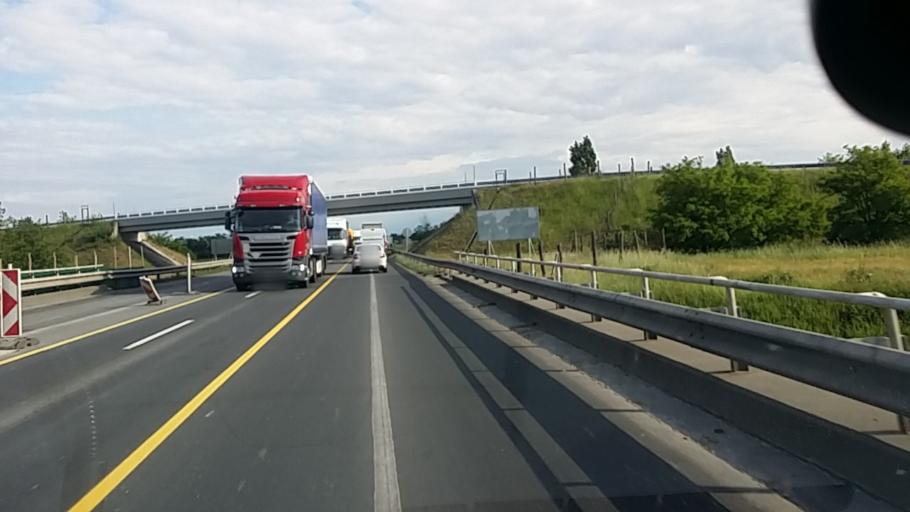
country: HU
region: Gyor-Moson-Sopron
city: Rajka
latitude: 47.9240
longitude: 17.1745
